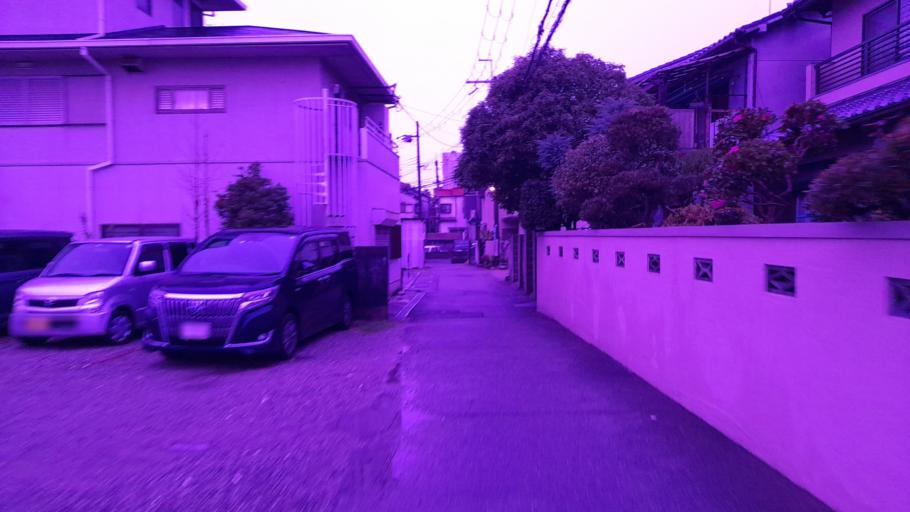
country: JP
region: Osaka
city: Toyonaka
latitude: 34.7449
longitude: 135.4506
